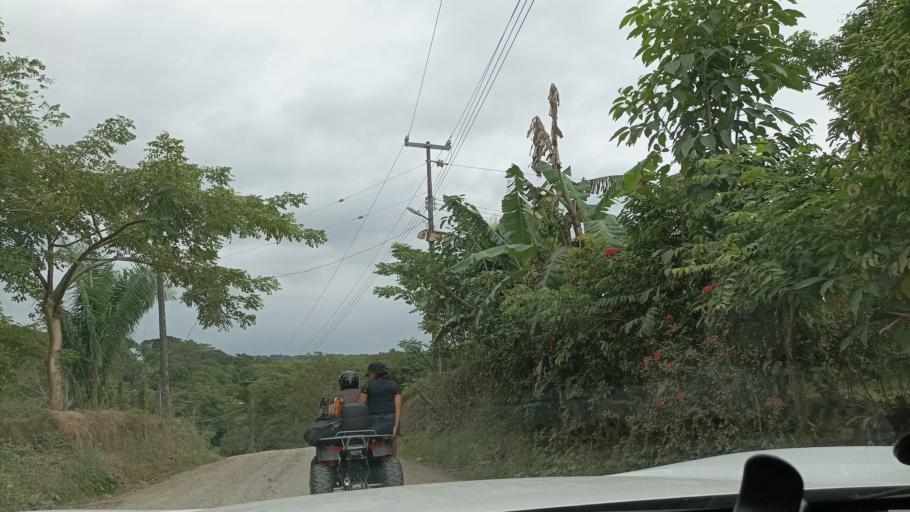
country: MX
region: Veracruz
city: Hidalgotitlan
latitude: 17.7766
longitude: -94.5182
